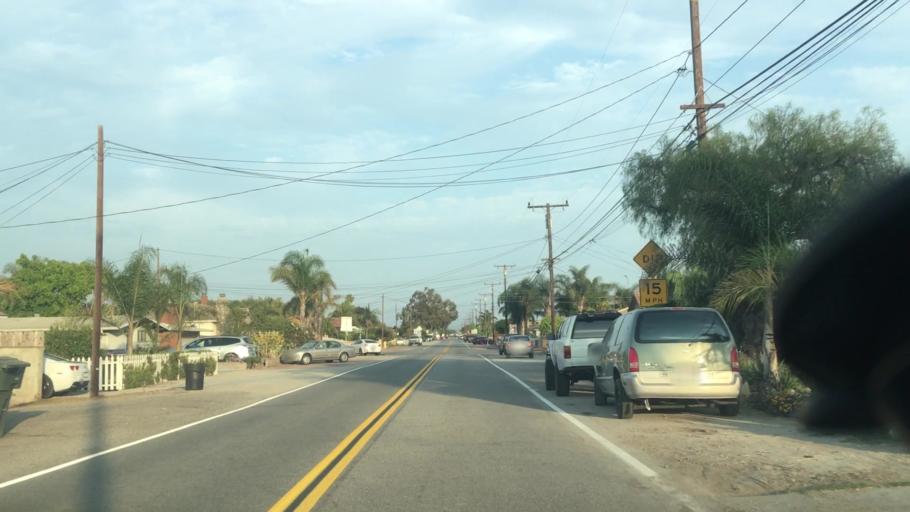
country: US
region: California
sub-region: Ventura County
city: El Rio
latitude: 34.2384
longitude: -119.1626
